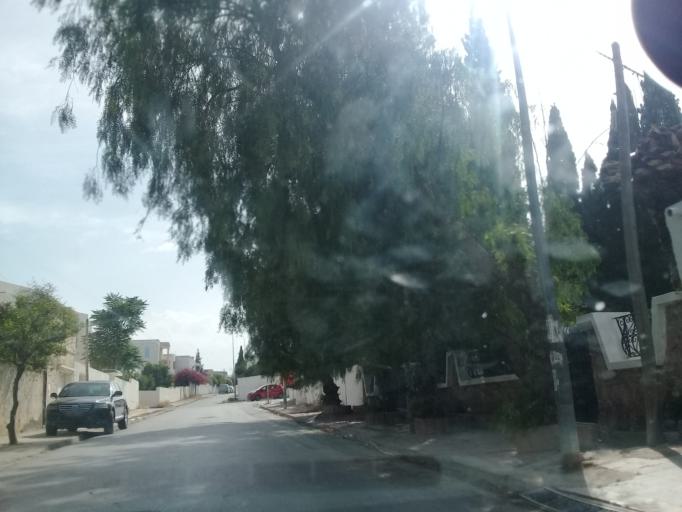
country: TN
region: Tunis
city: Tunis
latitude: 36.8521
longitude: 10.1606
